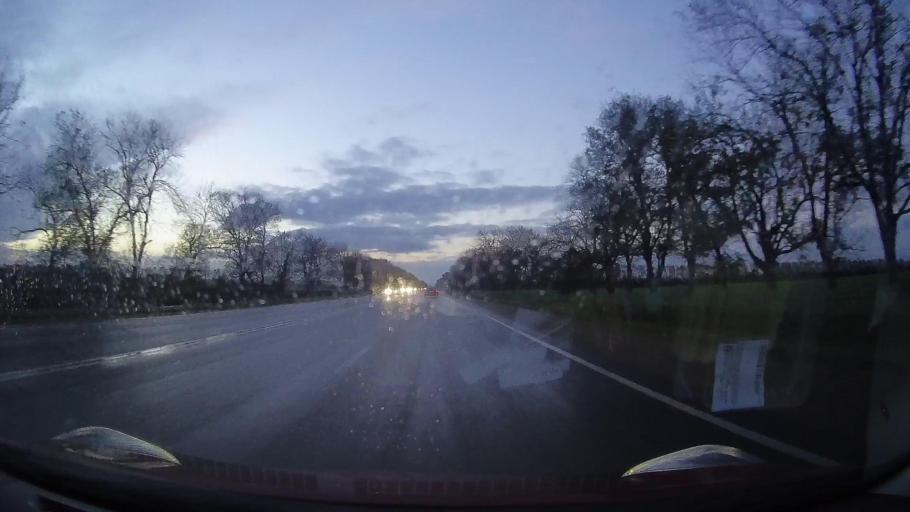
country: RU
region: Krasnodarskiy
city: Zavetnyy
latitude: 44.8878
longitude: 41.2132
